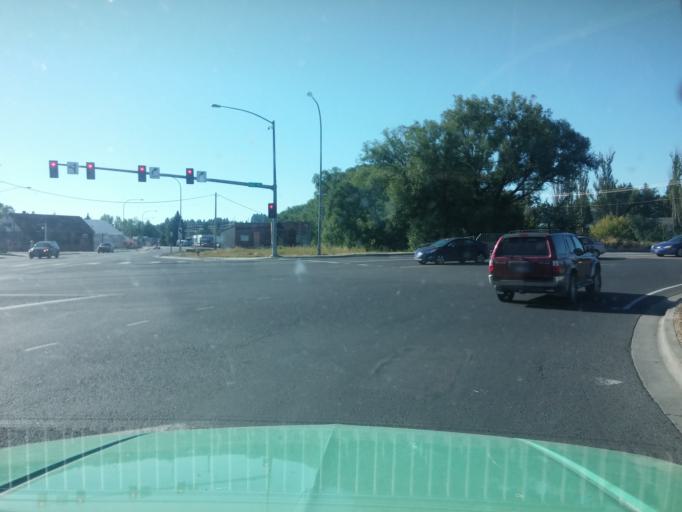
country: US
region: Idaho
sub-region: Latah County
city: Moscow
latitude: 46.7263
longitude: -117.0004
